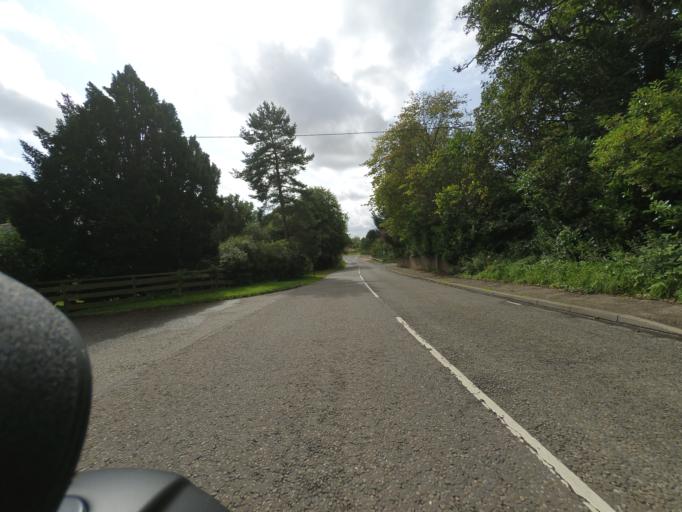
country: GB
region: Scotland
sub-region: Highland
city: Tain
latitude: 57.7471
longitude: -4.0731
